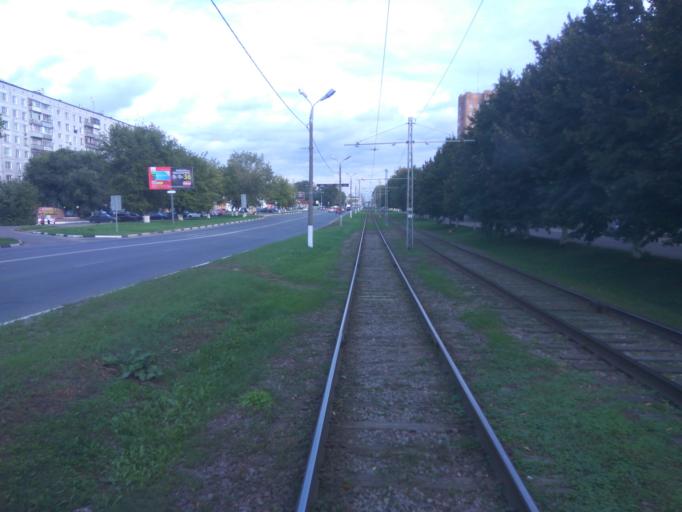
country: RU
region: Moskovskaya
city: Kolomna
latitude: 55.0872
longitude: 38.7918
